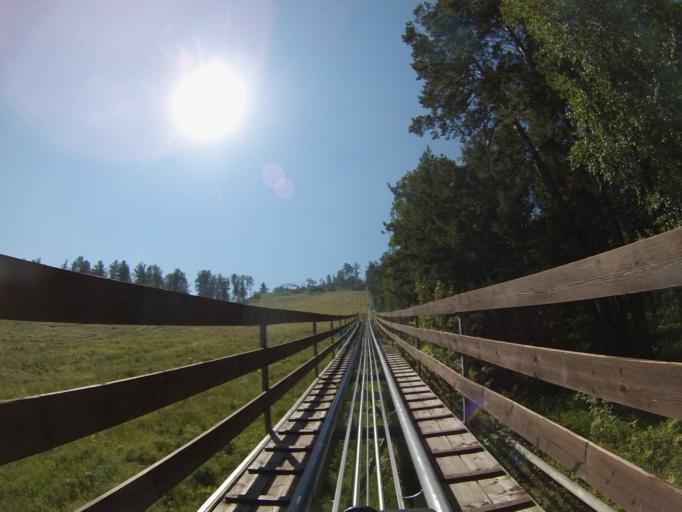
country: RU
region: Krasnoyarskiy
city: Krasnoyarsk
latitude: 55.9583
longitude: 92.7878
